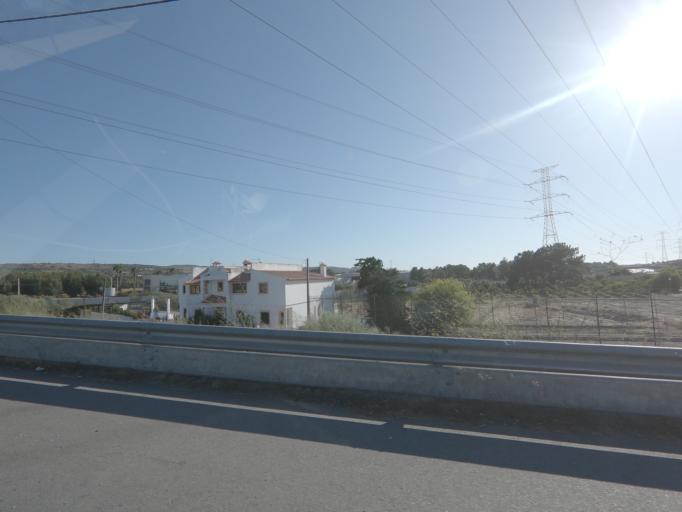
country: PT
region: Setubal
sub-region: Palmela
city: Palmela
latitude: 38.5865
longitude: -8.9169
